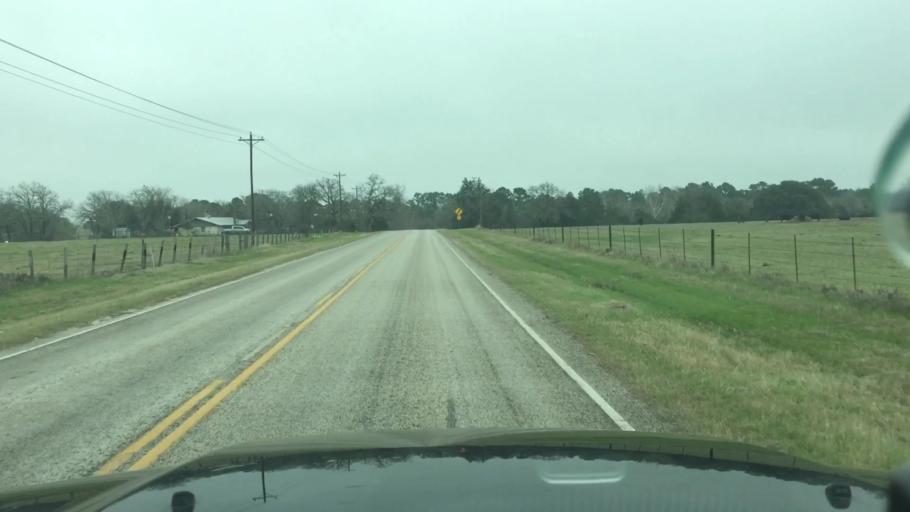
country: US
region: Texas
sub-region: Fayette County
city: La Grange
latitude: 30.0033
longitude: -96.9002
